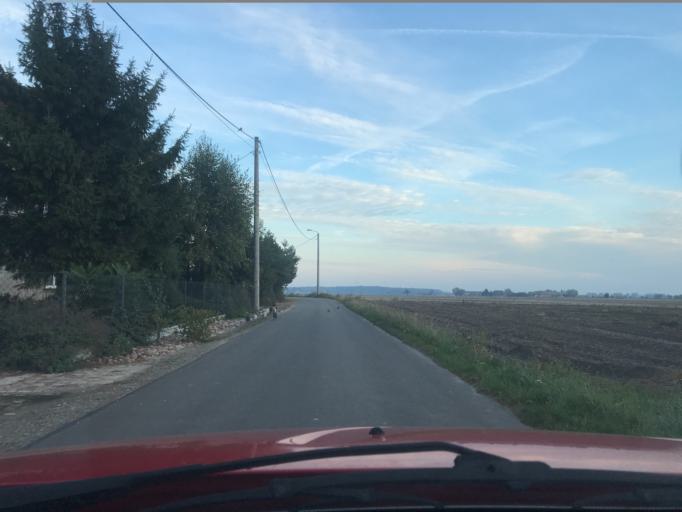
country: PL
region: Greater Poland Voivodeship
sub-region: Powiat ostrowski
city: Skalmierzyce
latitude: 51.7567
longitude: 17.9025
